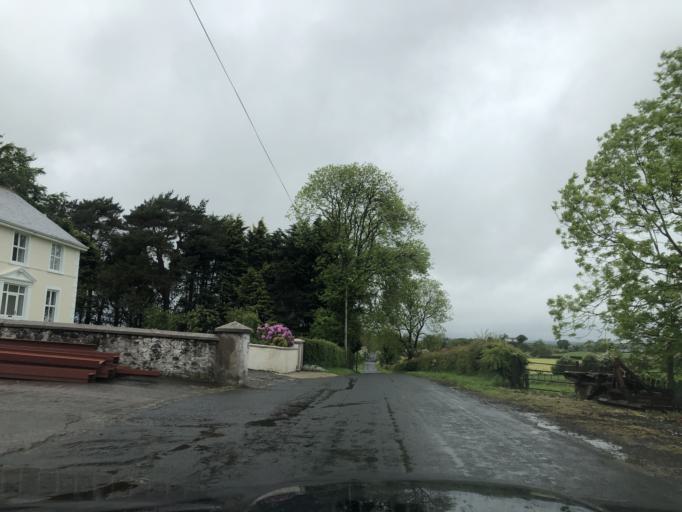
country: GB
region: Northern Ireland
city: Dunloy
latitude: 55.1134
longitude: -6.3479
